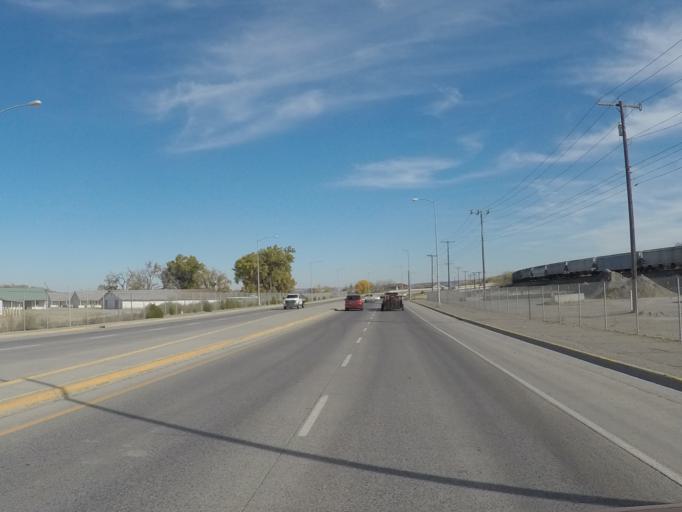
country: US
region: Montana
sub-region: Yellowstone County
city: Billings
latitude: 45.7956
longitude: -108.4760
